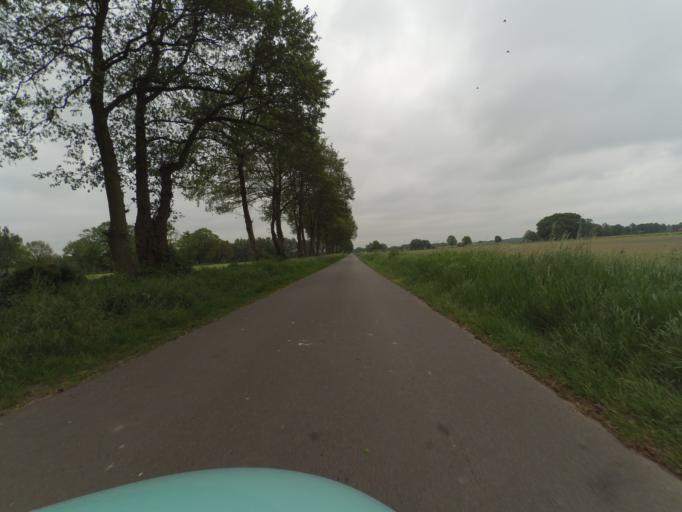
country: DE
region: Lower Saxony
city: Haenigsen
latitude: 52.4888
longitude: 10.1333
